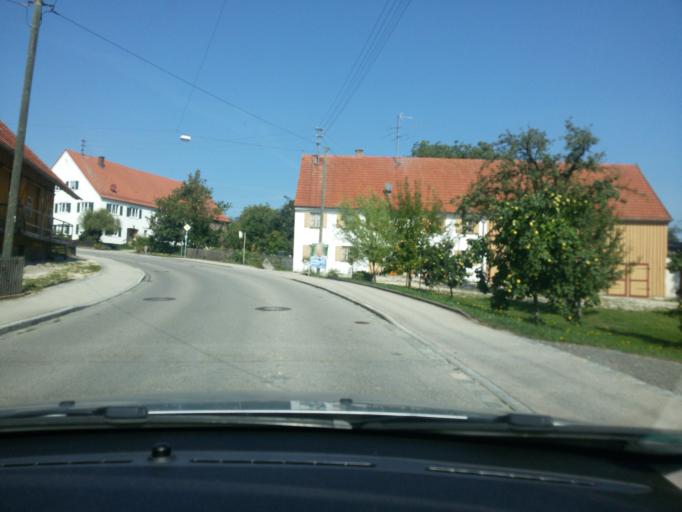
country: DE
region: Bavaria
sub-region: Swabia
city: Scherstetten
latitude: 48.2051
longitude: 10.6504
